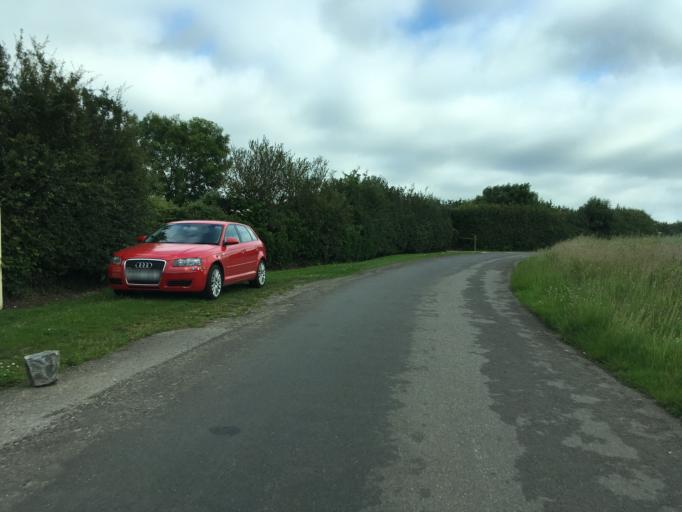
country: GB
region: England
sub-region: South Gloucestershire
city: Horton
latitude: 51.5686
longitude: -2.3553
